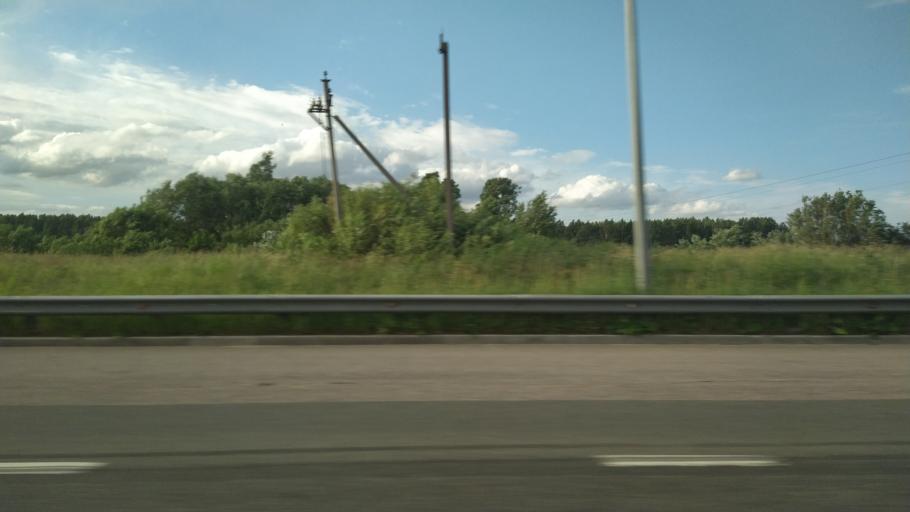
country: RU
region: St.-Petersburg
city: Krasnogvargeisky
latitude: 59.9879
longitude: 30.4711
